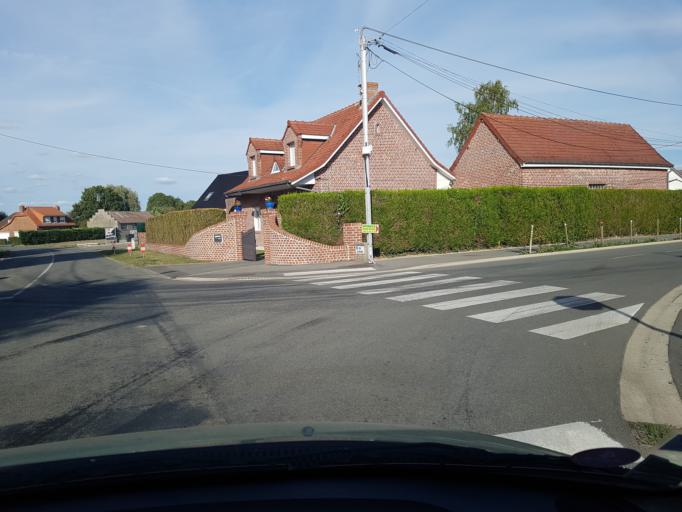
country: FR
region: Nord-Pas-de-Calais
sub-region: Departement du Pas-de-Calais
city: Hinges
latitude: 50.5914
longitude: 2.6330
